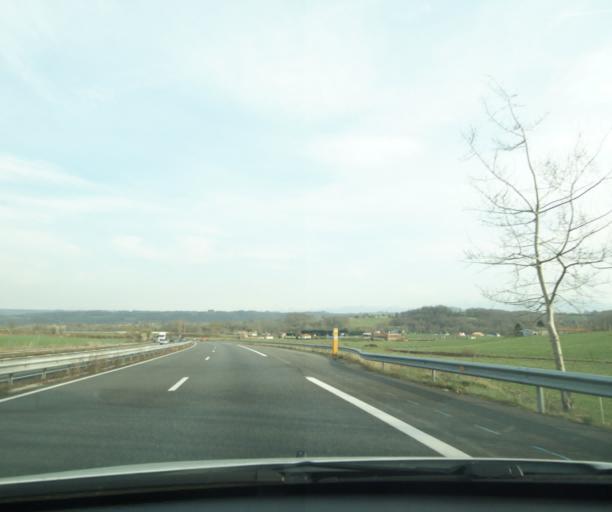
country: FR
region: Midi-Pyrenees
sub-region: Departement des Hautes-Pyrenees
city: Barbazan-Debat
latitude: 43.2006
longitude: 0.1508
